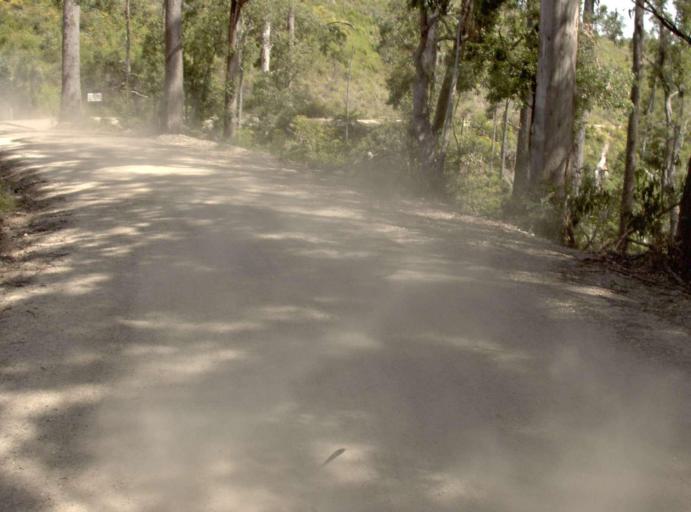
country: AU
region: Victoria
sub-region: East Gippsland
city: Lakes Entrance
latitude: -37.6040
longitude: 148.7099
